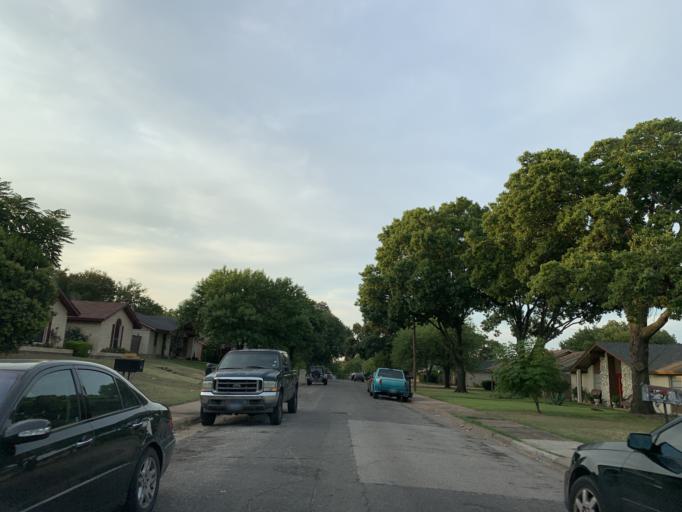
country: US
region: Texas
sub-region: Dallas County
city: Cockrell Hill
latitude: 32.7011
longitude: -96.8882
